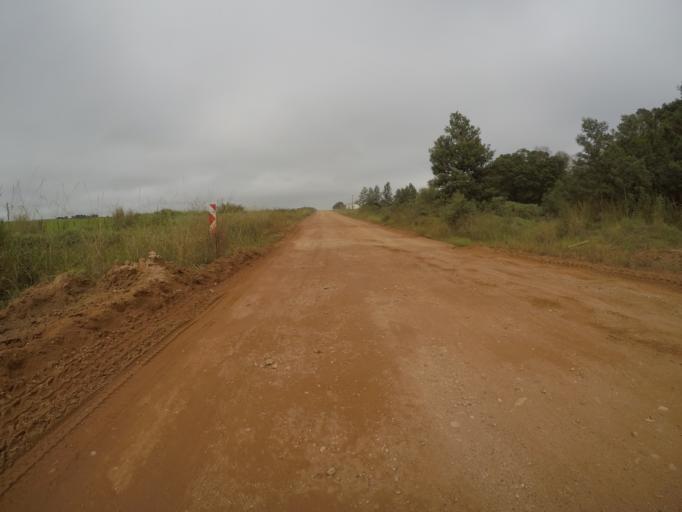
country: ZA
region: Eastern Cape
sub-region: Cacadu District Municipality
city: Kareedouw
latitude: -34.0148
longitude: 24.2380
